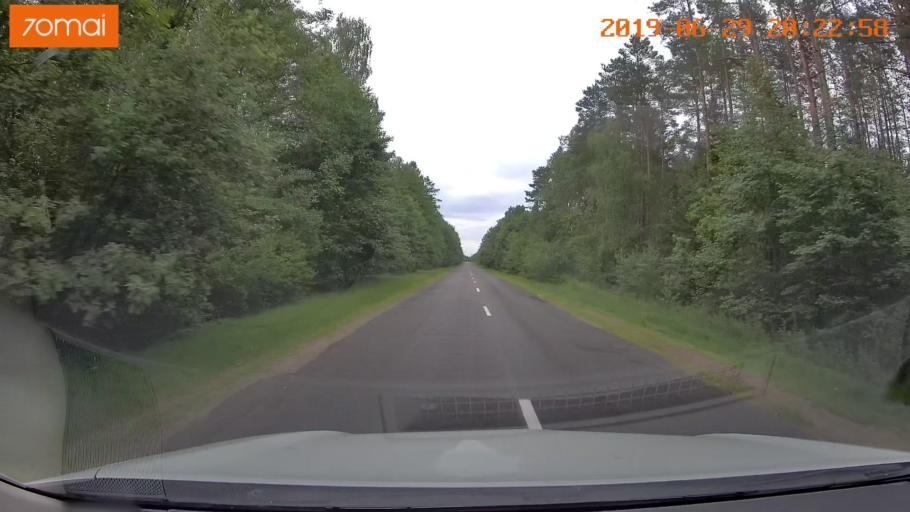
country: BY
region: Brest
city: Asnyezhytsy
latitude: 52.4384
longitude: 26.2576
